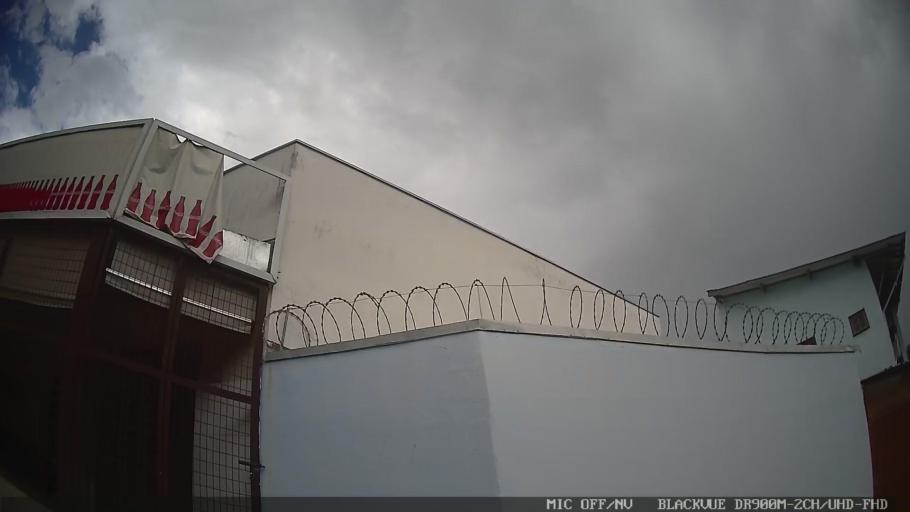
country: BR
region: Sao Paulo
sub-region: Jaguariuna
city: Jaguariuna
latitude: -22.6993
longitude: -47.0185
